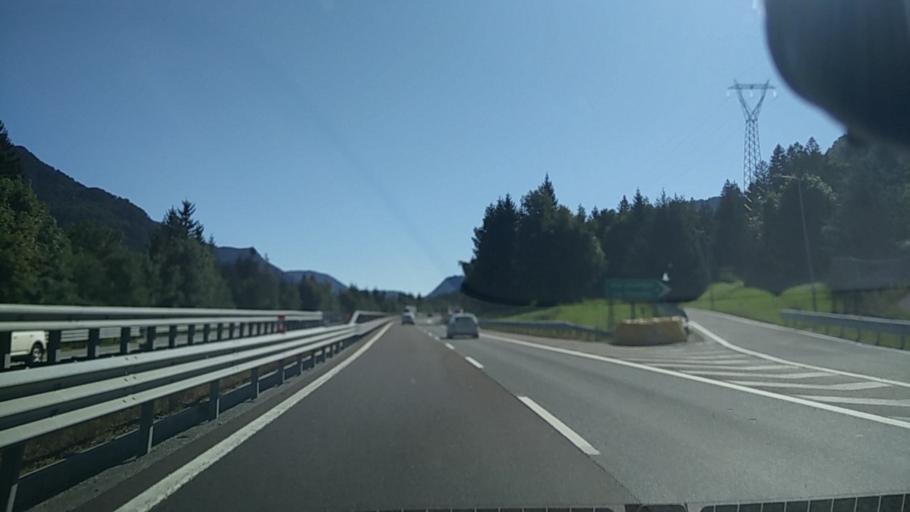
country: IT
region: Friuli Venezia Giulia
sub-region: Provincia di Udine
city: Malborghetto
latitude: 46.4980
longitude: 13.3847
